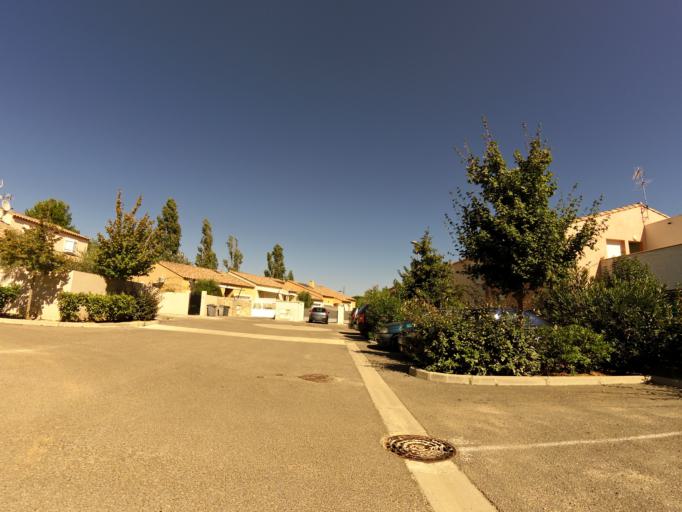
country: FR
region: Languedoc-Roussillon
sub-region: Departement du Gard
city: Vergeze
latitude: 43.7395
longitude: 4.2265
